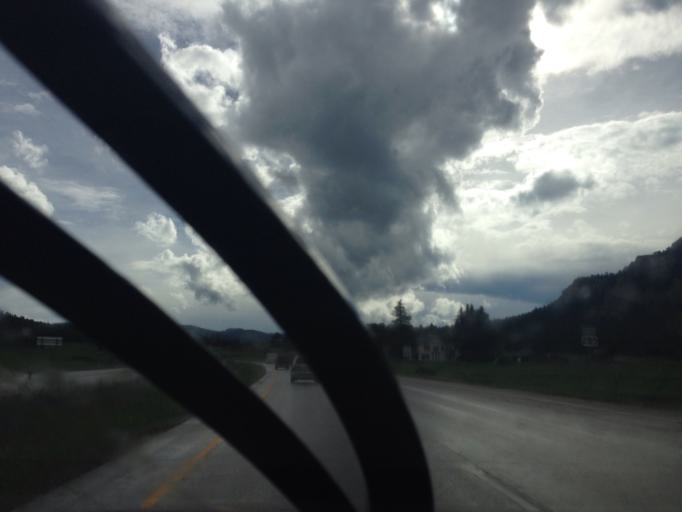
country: US
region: Colorado
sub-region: Jefferson County
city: Indian Hills
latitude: 39.5466
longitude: -105.2751
